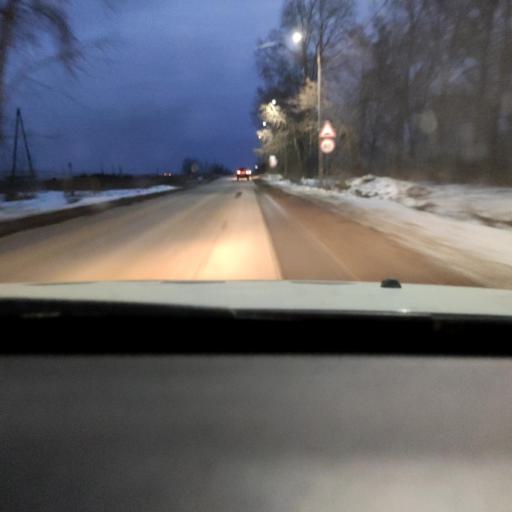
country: RU
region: Perm
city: Gamovo
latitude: 57.8741
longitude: 56.1020
